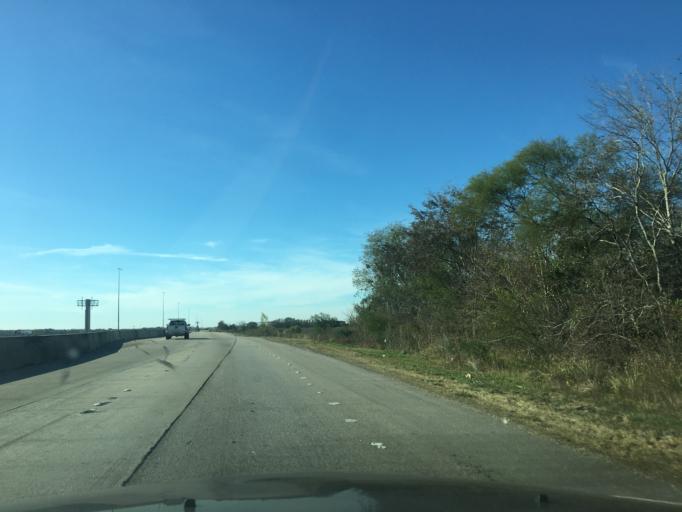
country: US
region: Texas
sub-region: Fort Bend County
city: Rosenberg
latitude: 29.5326
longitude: -95.8253
